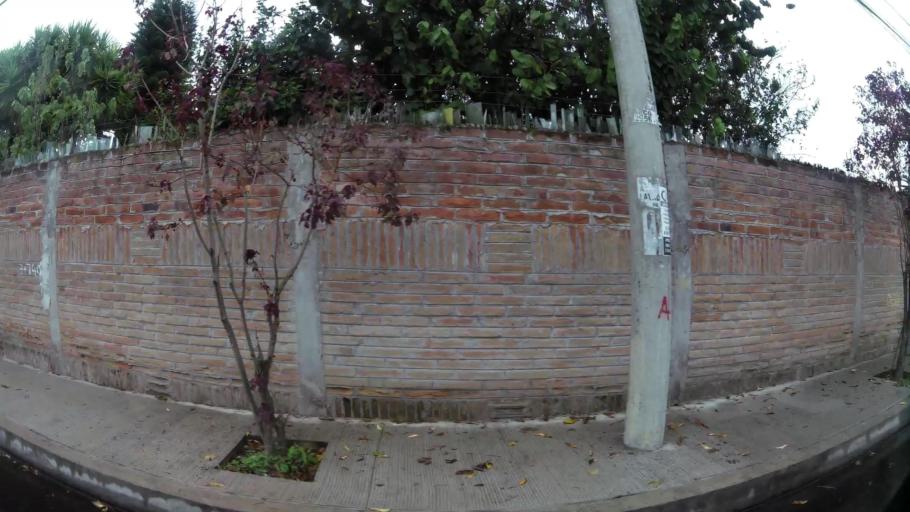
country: EC
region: Pichincha
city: Sangolqui
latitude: -0.2877
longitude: -78.4551
